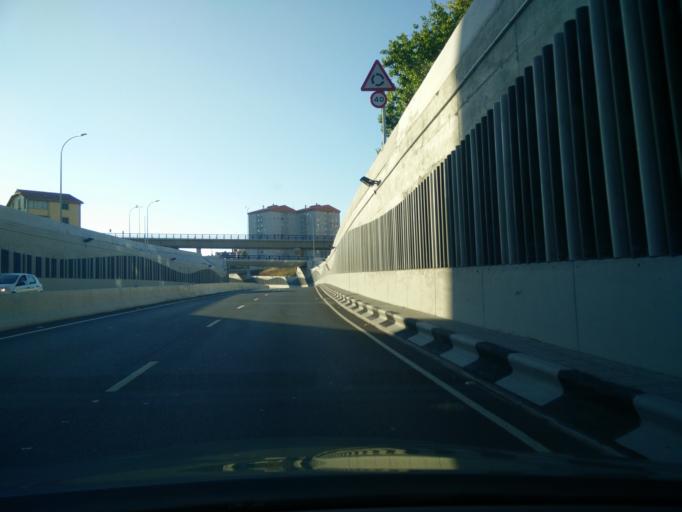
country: ES
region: Galicia
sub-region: Provincia da Coruna
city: A Coruna
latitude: 43.3437
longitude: -8.4139
